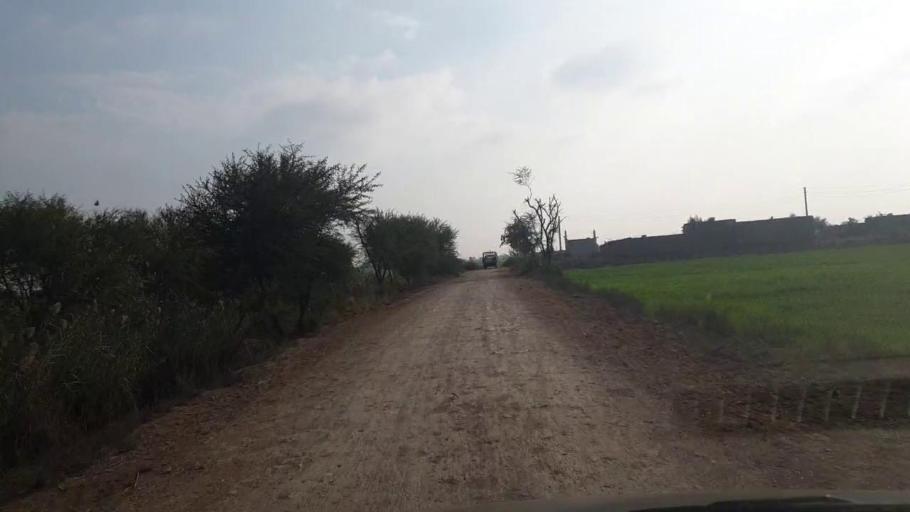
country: PK
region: Sindh
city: Shahdadpur
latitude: 25.8712
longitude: 68.6635
